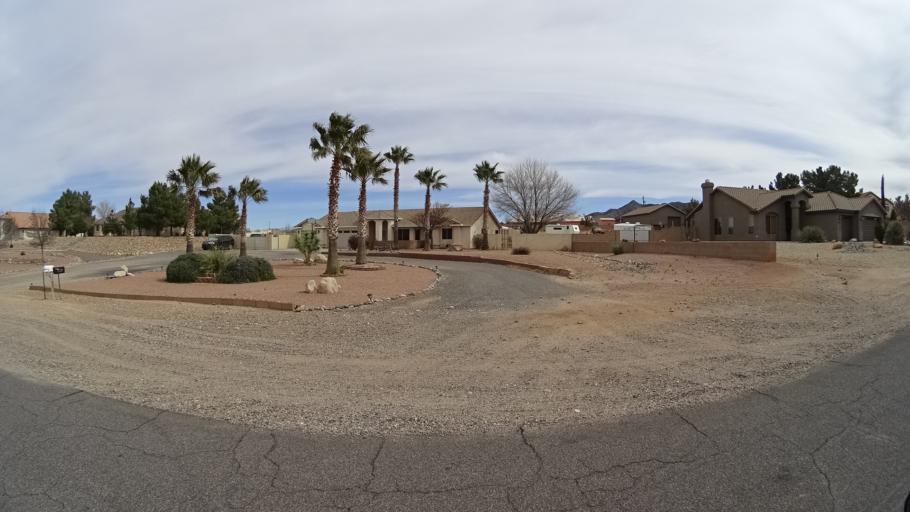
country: US
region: Arizona
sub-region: Mohave County
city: Kingman
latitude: 35.1944
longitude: -113.9928
